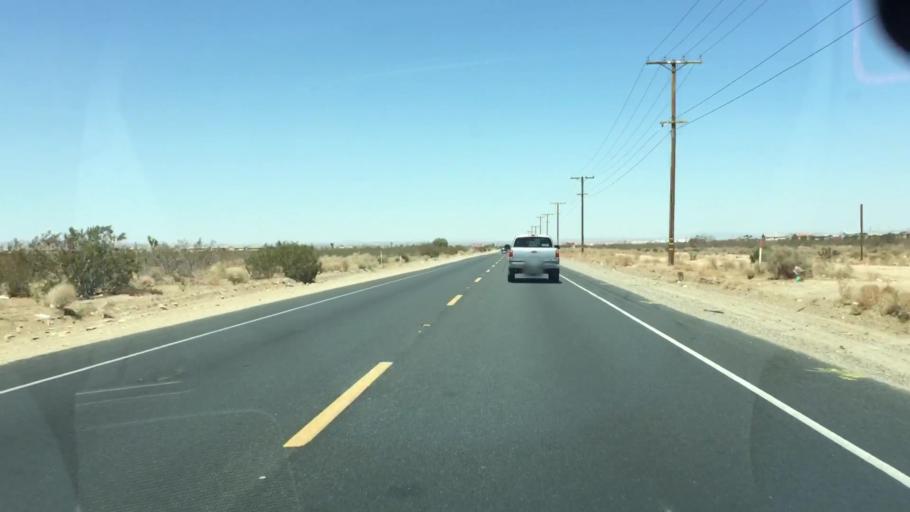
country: US
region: California
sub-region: San Bernardino County
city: Mountain View Acres
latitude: 34.4810
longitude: -117.3995
